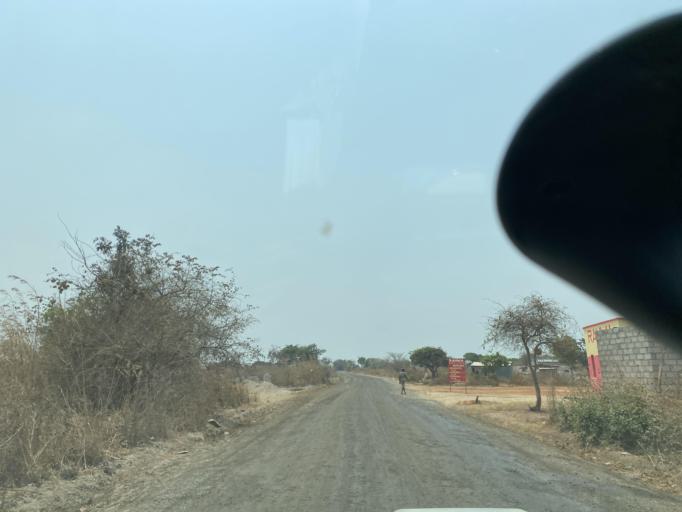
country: ZM
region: Lusaka
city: Lusaka
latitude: -15.5500
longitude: 28.4447
